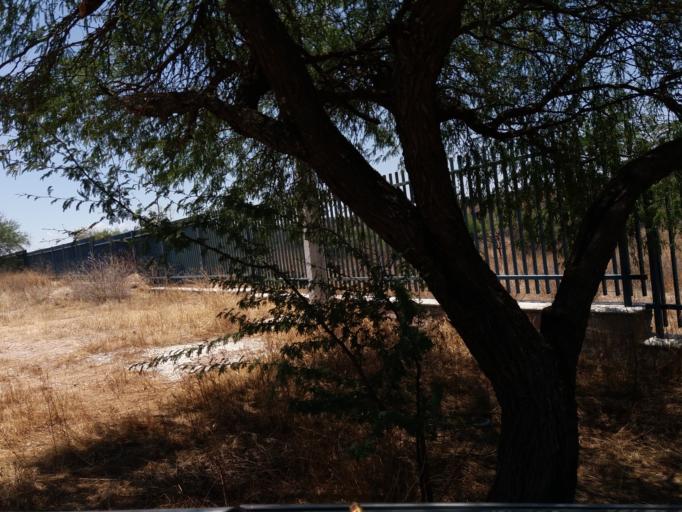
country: MX
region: Aguascalientes
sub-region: Aguascalientes
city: San Sebastian [Fraccionamiento]
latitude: 21.7903
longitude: -102.2984
